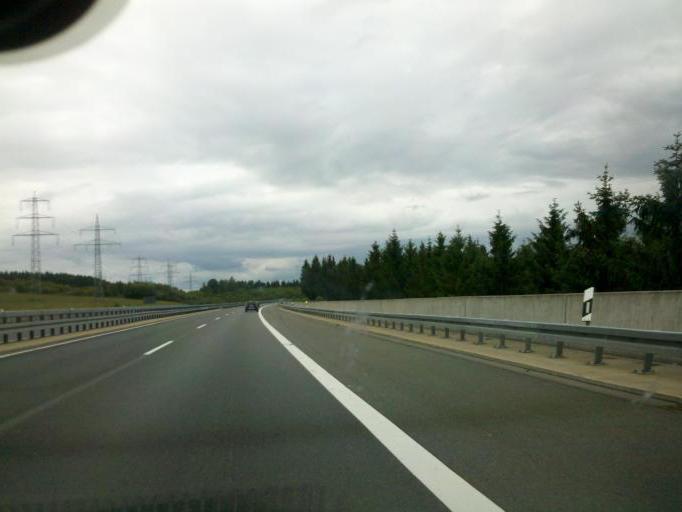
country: DE
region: North Rhine-Westphalia
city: Kreuztal
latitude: 50.9854
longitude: 7.9380
